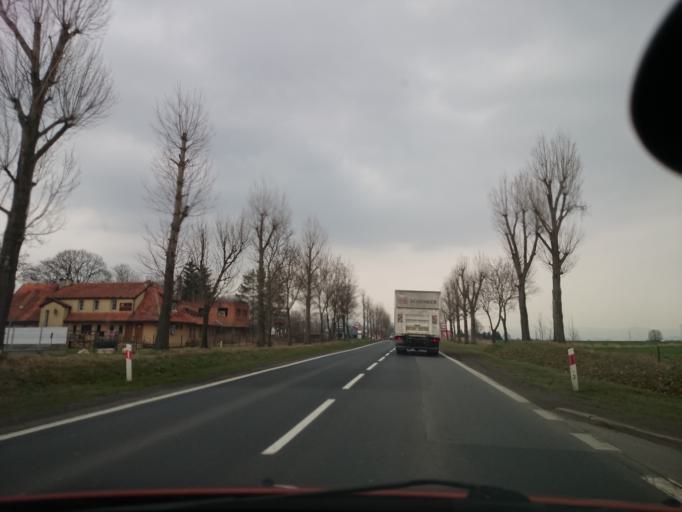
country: PL
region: Lower Silesian Voivodeship
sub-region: Powiat klodzki
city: Klodzko
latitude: 50.4375
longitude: 16.6085
